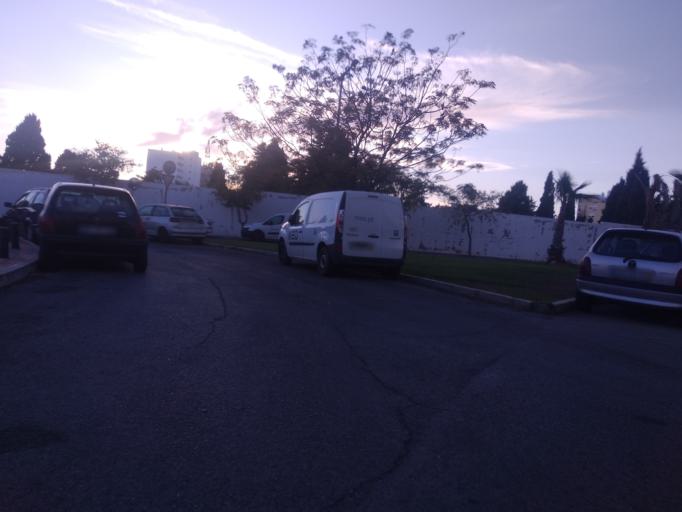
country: PT
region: Faro
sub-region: Faro
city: Faro
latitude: 37.0220
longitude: -7.9310
